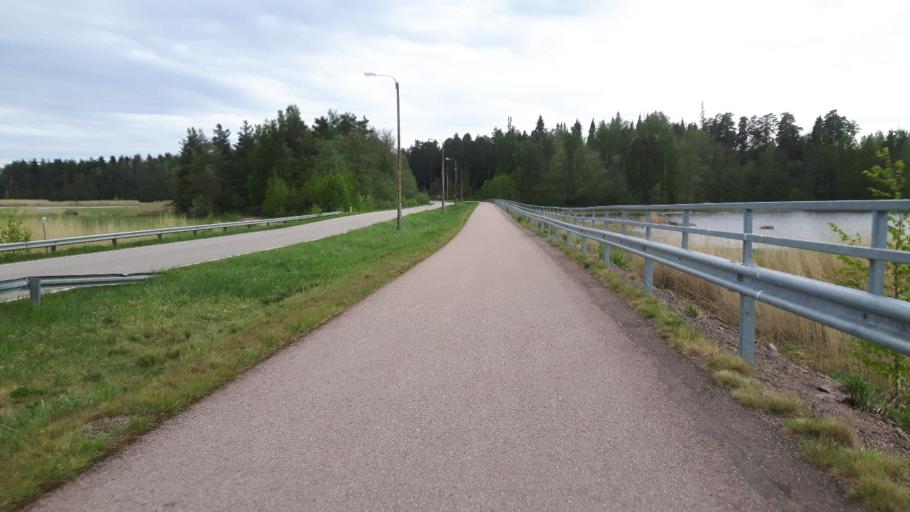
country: FI
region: Kymenlaakso
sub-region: Kotka-Hamina
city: Hamina
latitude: 60.5497
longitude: 27.2283
